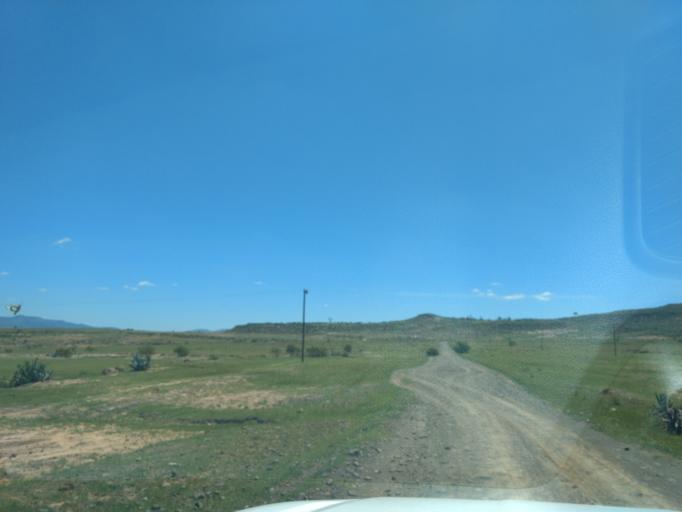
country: LS
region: Maseru
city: Maseru
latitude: -29.4739
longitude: 27.3751
